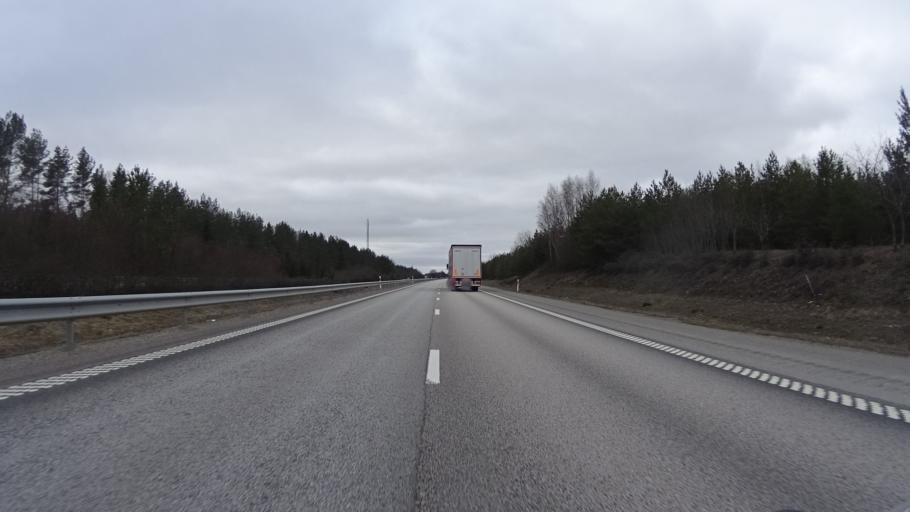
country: SE
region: Soedermanland
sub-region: Strangnas Kommun
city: Mariefred
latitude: 59.2227
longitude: 17.2698
